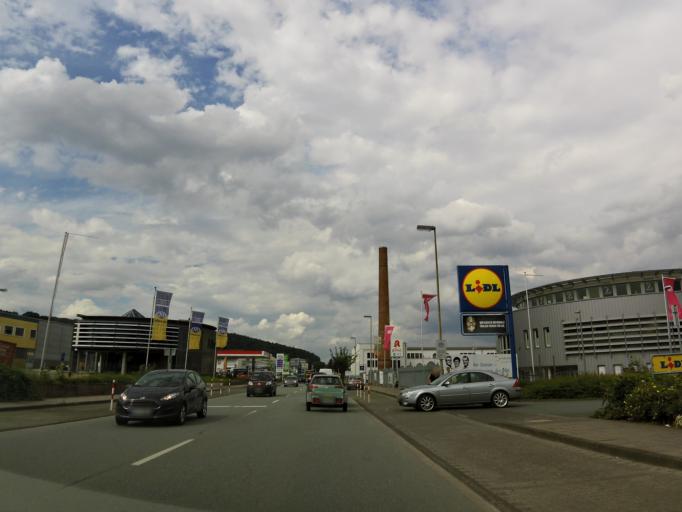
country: DE
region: North Rhine-Westphalia
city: Beverungen
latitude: 51.6731
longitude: 9.3754
